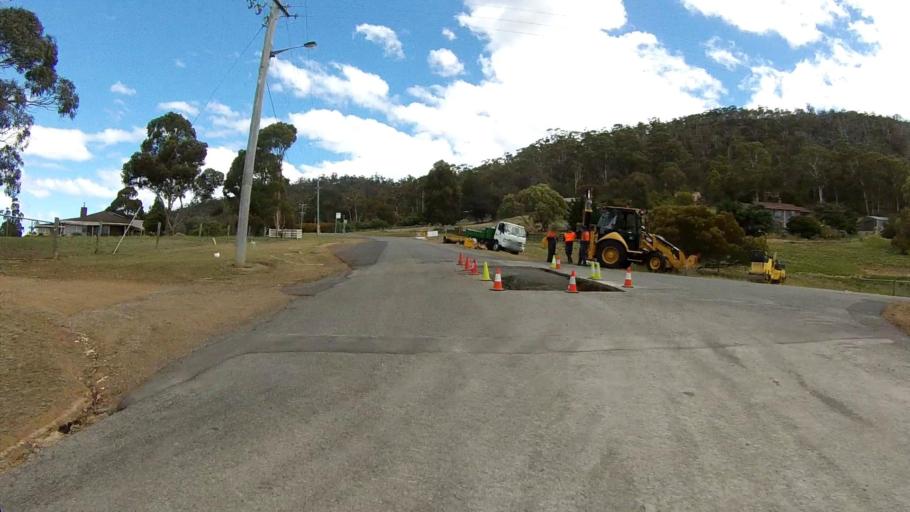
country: AU
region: Tasmania
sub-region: Clarence
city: Acton Park
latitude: -42.8616
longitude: 147.4709
